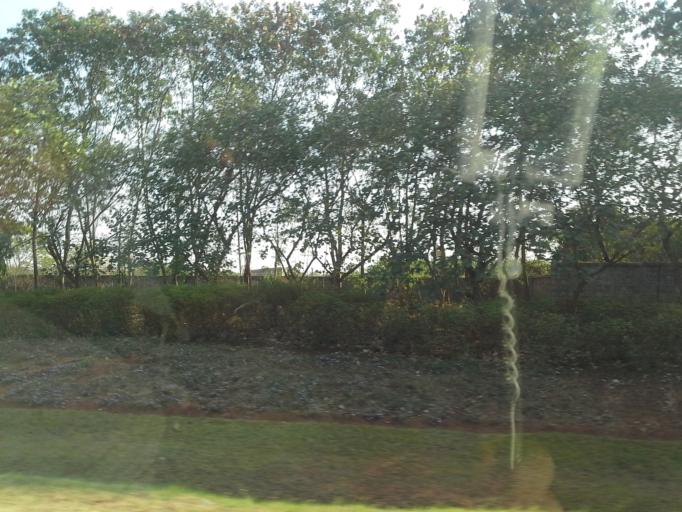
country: IN
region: Telangana
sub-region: Rangareddi
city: Balapur
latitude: 17.2444
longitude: 78.3921
